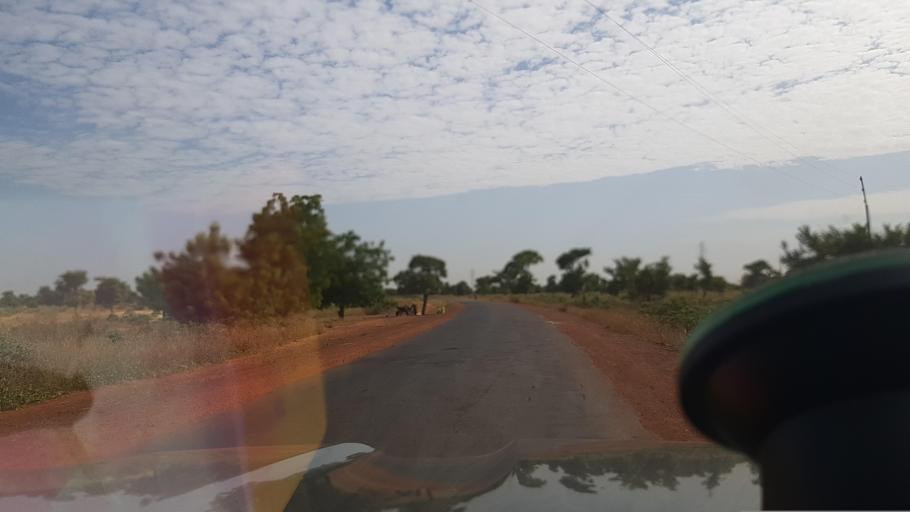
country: ML
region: Segou
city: Segou
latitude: 13.5001
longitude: -6.1523
